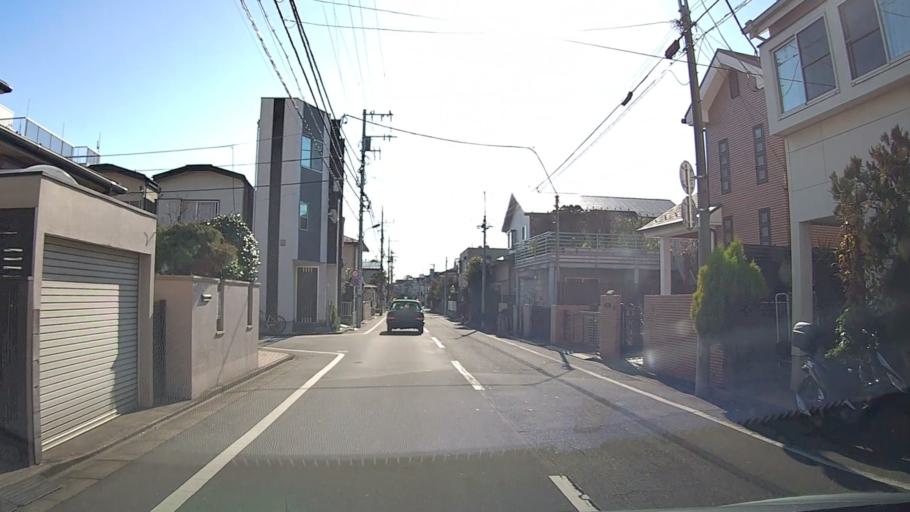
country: JP
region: Tokyo
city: Tokyo
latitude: 35.7340
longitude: 139.6567
